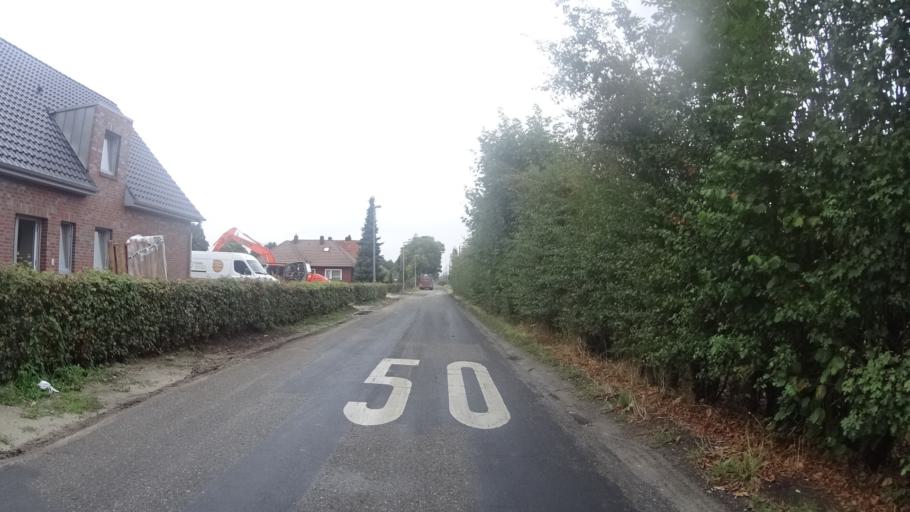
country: DE
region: Lower Saxony
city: Leer
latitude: 53.2394
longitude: 7.4649
